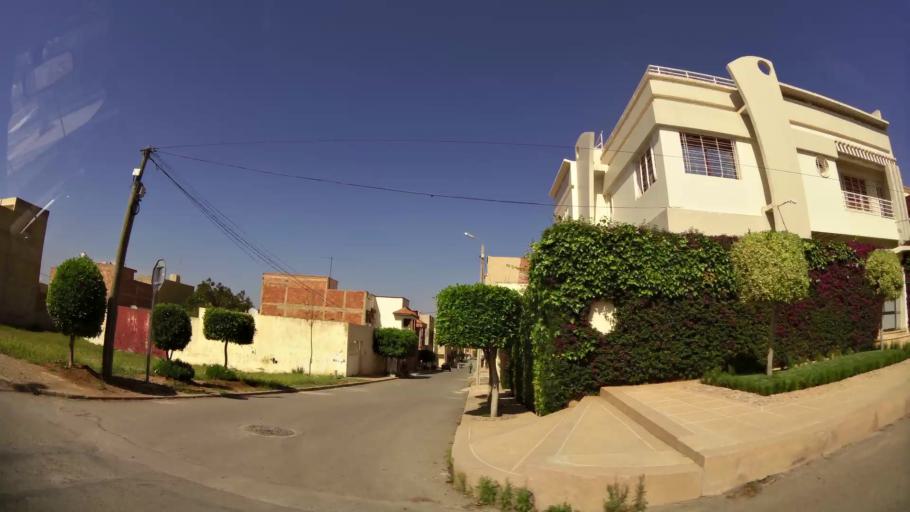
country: MA
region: Oriental
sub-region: Oujda-Angad
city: Oujda
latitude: 34.6918
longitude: -1.8791
